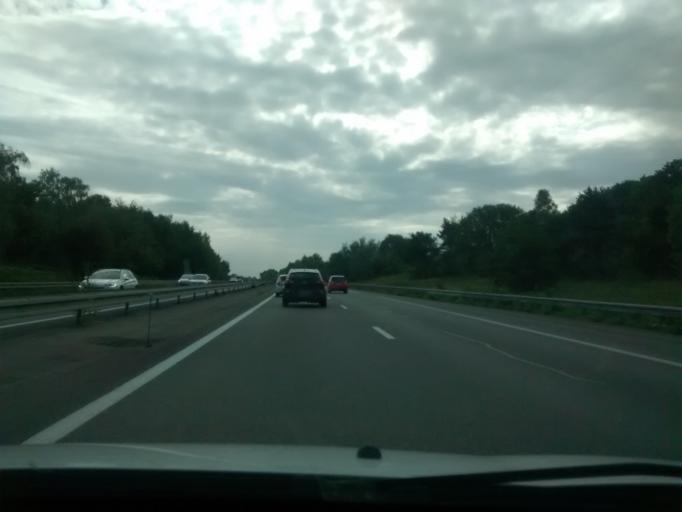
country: FR
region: Pays de la Loire
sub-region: Departement de la Mayenne
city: Port-Brillet
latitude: 48.0770
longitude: -0.9900
